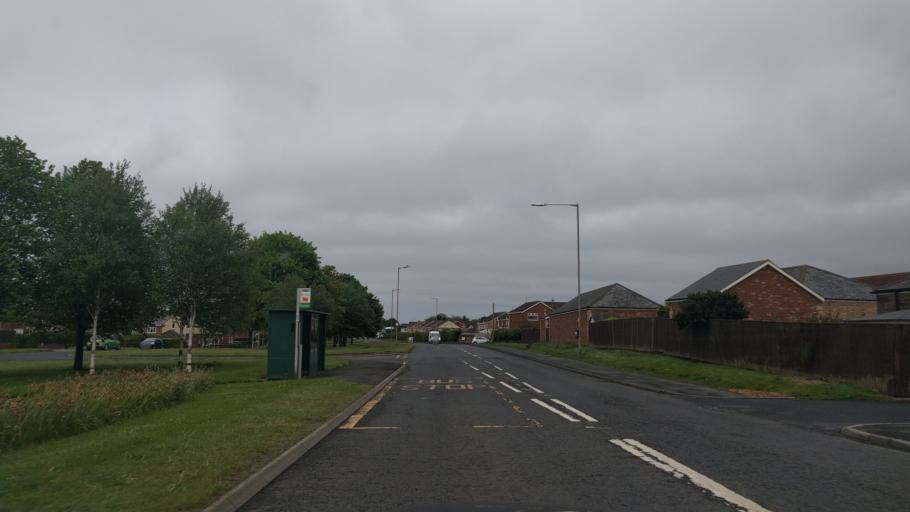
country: GB
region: England
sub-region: Northumberland
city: Choppington
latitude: 55.1592
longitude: -1.6109
